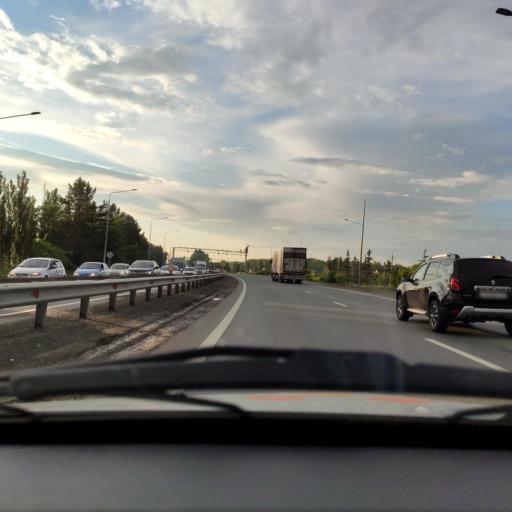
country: RU
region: Bashkortostan
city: Ufa
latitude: 54.5589
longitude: 55.9241
